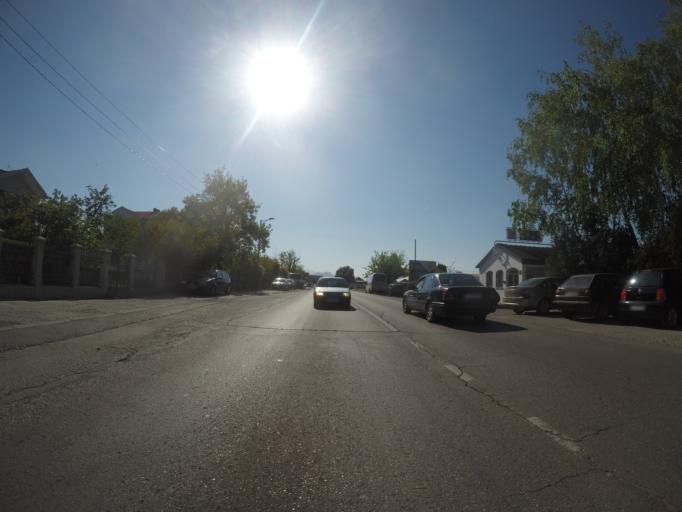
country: ME
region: Podgorica
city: Podgorica
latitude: 42.4403
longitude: 19.2186
